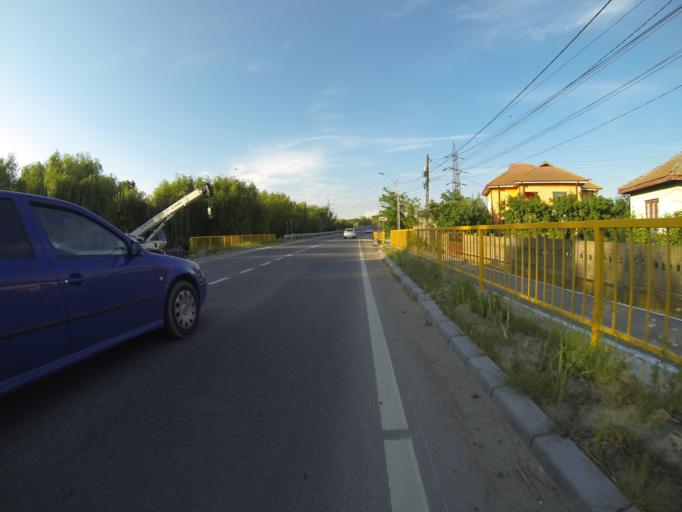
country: RO
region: Dolj
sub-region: Comuna Podari
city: Podari
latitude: 44.2576
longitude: 23.7804
